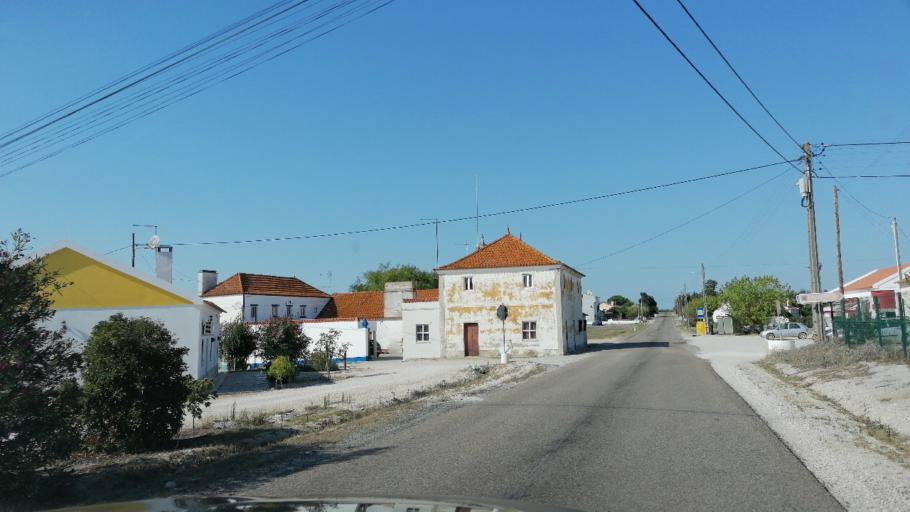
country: PT
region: Santarem
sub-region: Coruche
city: Coruche
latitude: 38.8244
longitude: -8.5659
